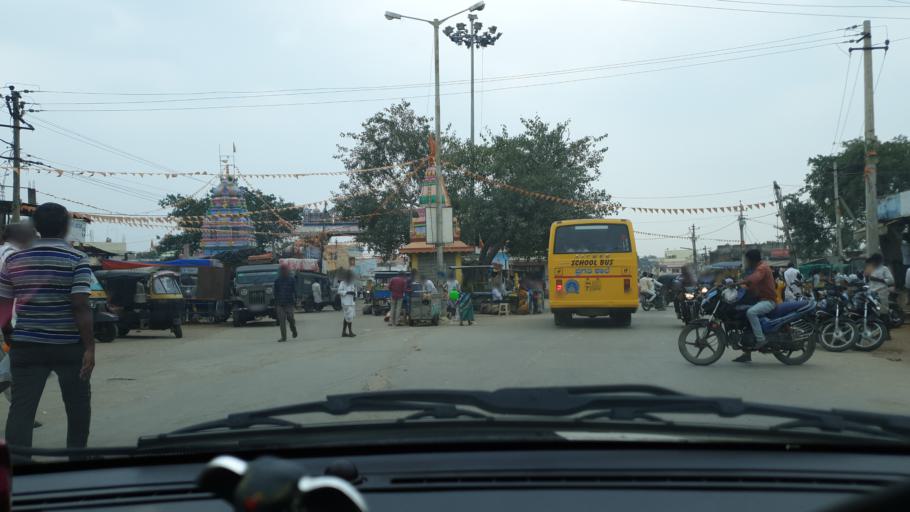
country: IN
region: Karnataka
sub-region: Yadgir
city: Gurmatkal
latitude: 16.8714
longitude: 77.3912
